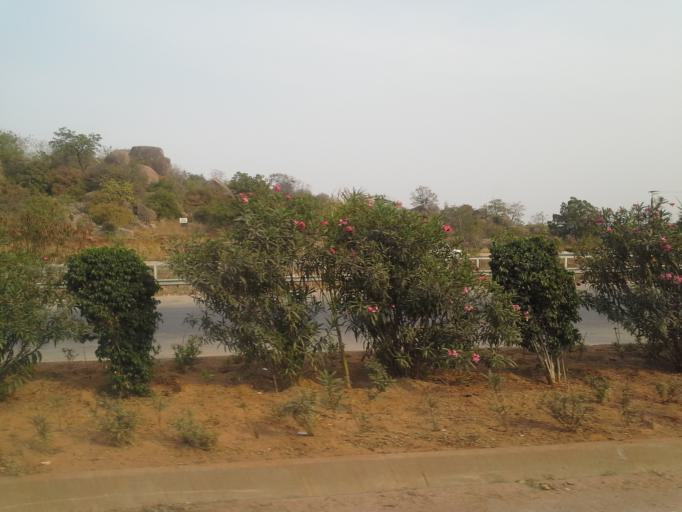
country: IN
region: Telangana
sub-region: Rangareddi
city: Kukatpalli
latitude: 17.4095
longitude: 78.3543
